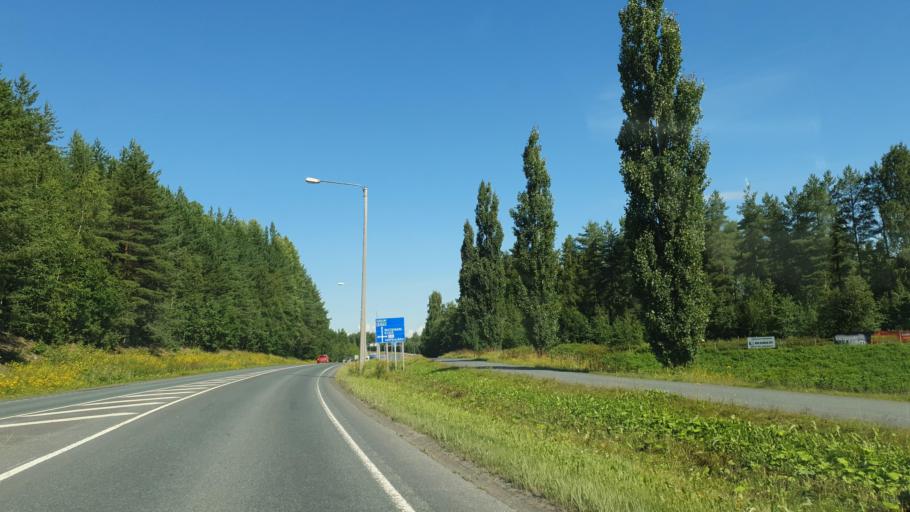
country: FI
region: Northern Savo
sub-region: Ylae-Savo
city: Lapinlahti
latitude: 63.3490
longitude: 27.4144
